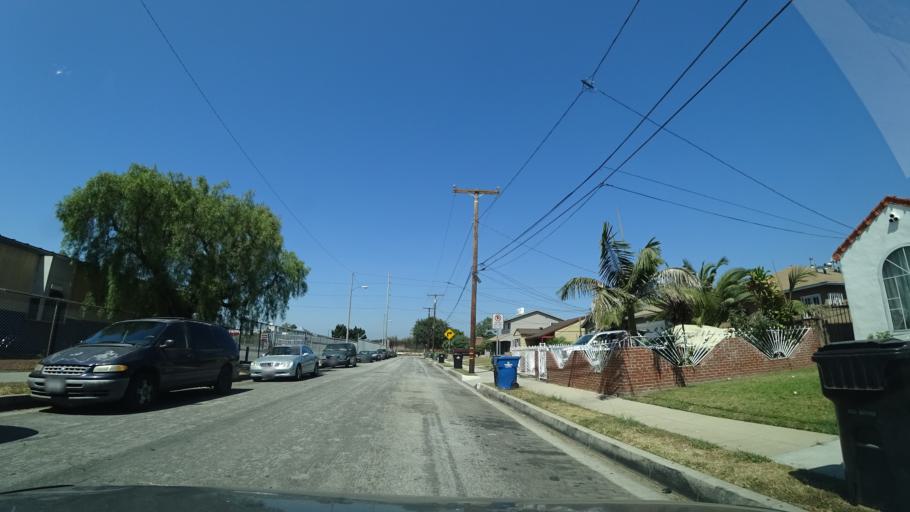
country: US
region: California
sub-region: Los Angeles County
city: Inglewood
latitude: 33.9558
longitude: -118.3674
